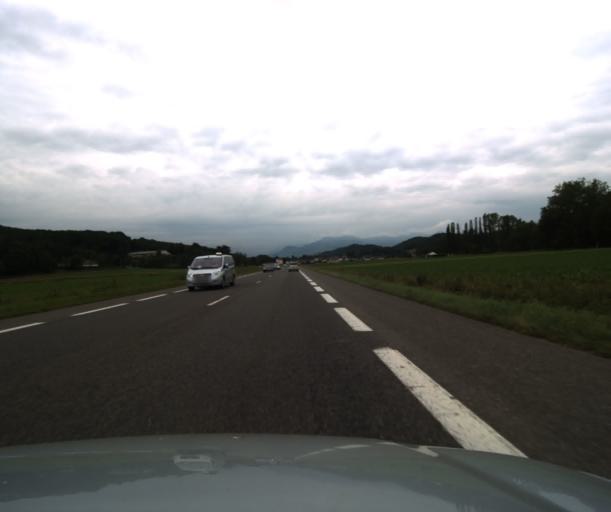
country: FR
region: Midi-Pyrenees
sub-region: Departement des Hautes-Pyrenees
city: Ossun
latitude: 43.1485
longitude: -0.0237
